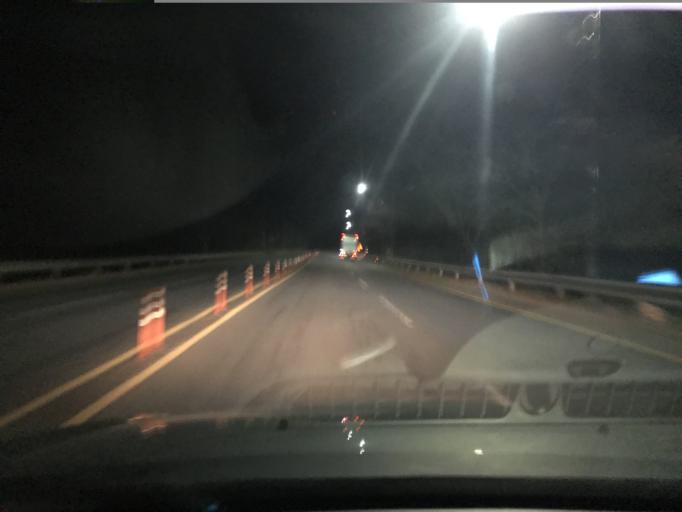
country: KR
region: Daegu
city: Hwawon
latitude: 35.7322
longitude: 128.4771
